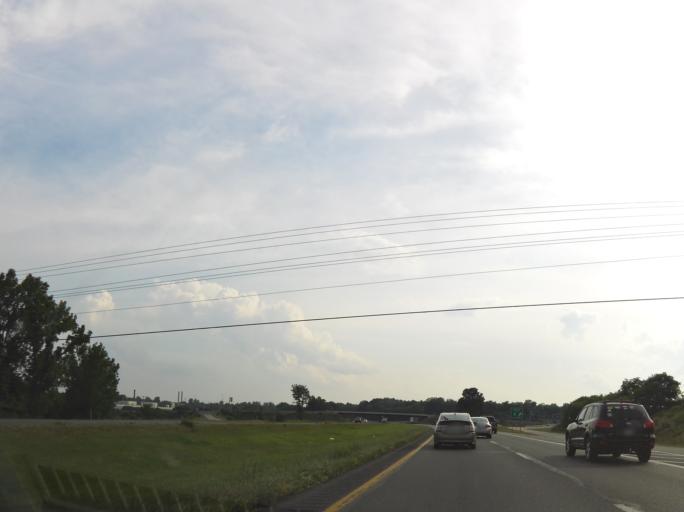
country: US
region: West Virginia
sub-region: Berkeley County
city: Inwood
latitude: 39.4098
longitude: -78.0213
